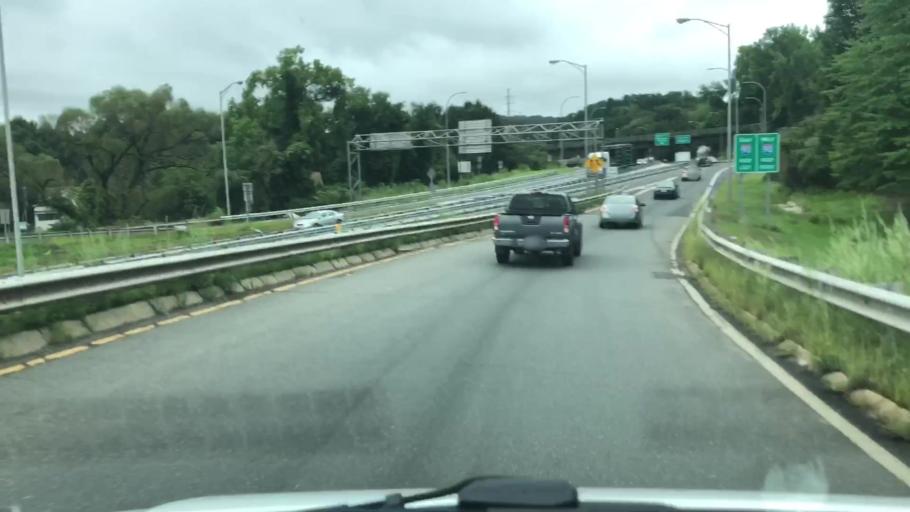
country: US
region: Massachusetts
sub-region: Hampden County
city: Chicopee
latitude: 42.1572
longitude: -72.6381
